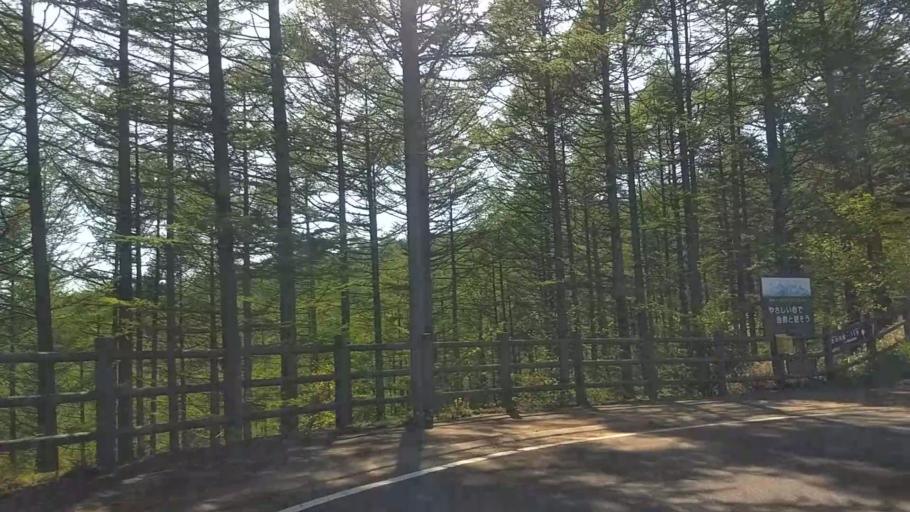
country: JP
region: Yamanashi
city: Nirasaki
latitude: 35.9214
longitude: 138.3979
